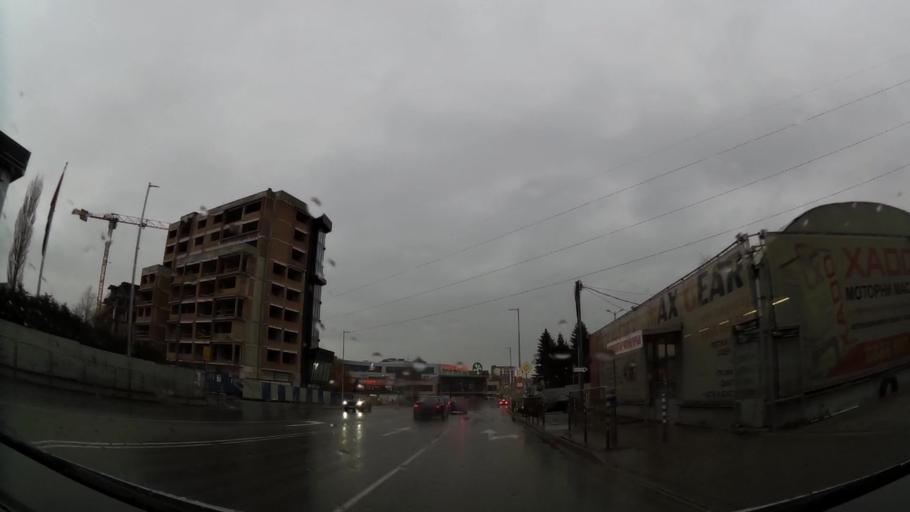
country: BG
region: Sofia-Capital
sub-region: Stolichna Obshtina
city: Sofia
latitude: 42.6545
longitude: 23.3158
